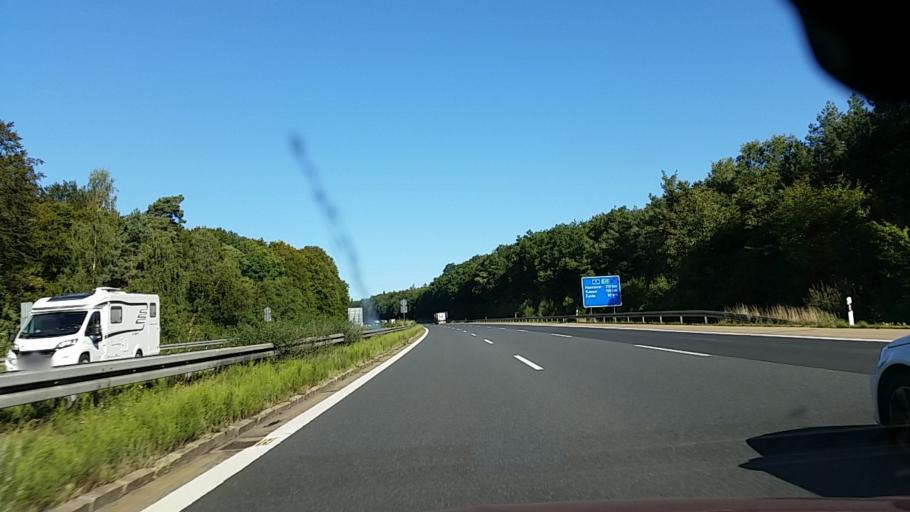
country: DE
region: Bavaria
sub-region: Regierungsbezirk Unterfranken
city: Oberthulba
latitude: 50.2018
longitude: 9.9369
